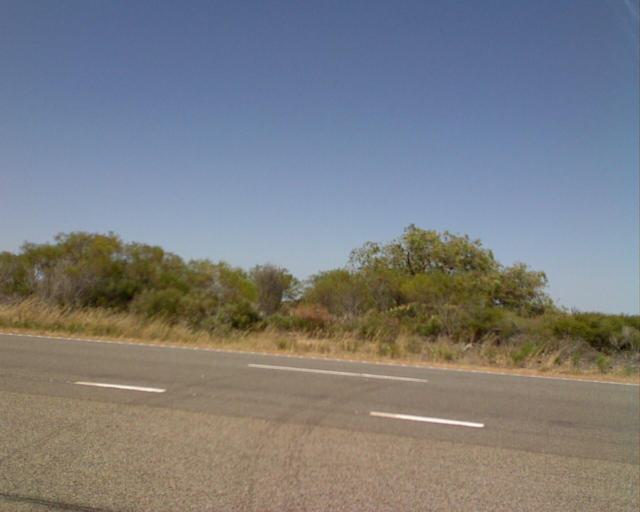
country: AU
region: Western Australia
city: Port Denison
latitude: -29.6571
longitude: 115.2272
